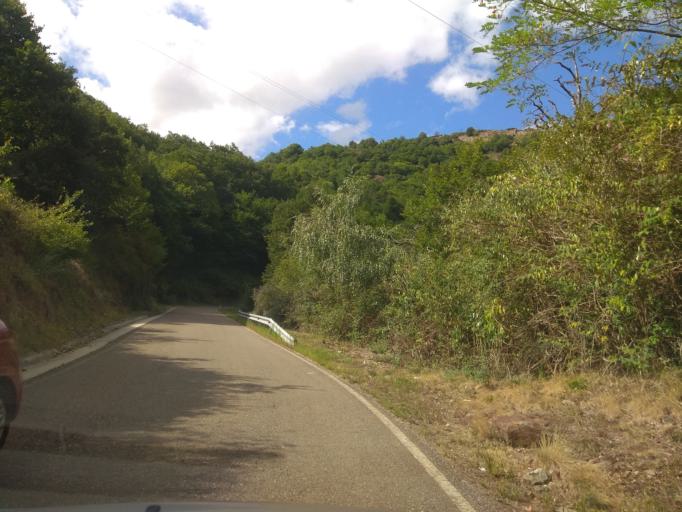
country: ES
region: Catalonia
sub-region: Provincia de Lleida
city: Les
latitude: 42.8286
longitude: 0.7258
